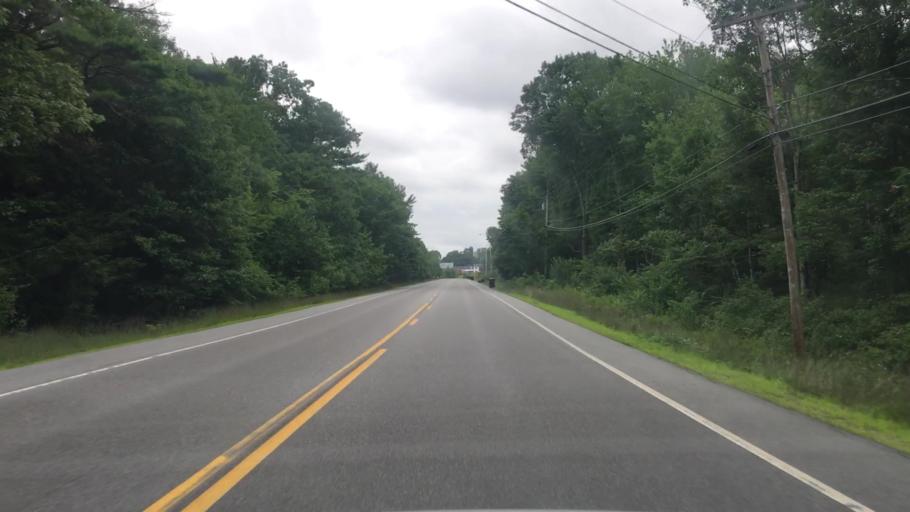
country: US
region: Maine
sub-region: York County
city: Biddeford
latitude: 43.5256
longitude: -70.4957
